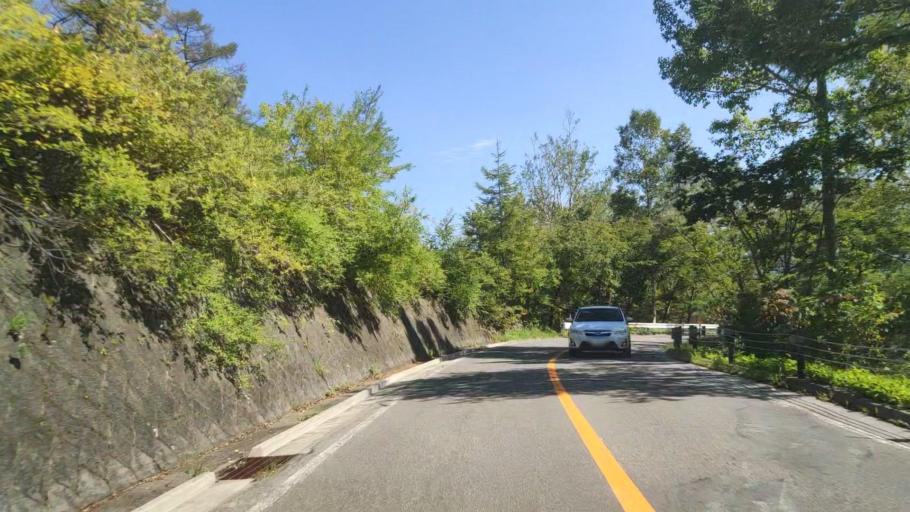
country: JP
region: Nagano
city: Nakano
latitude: 36.6293
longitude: 138.5667
